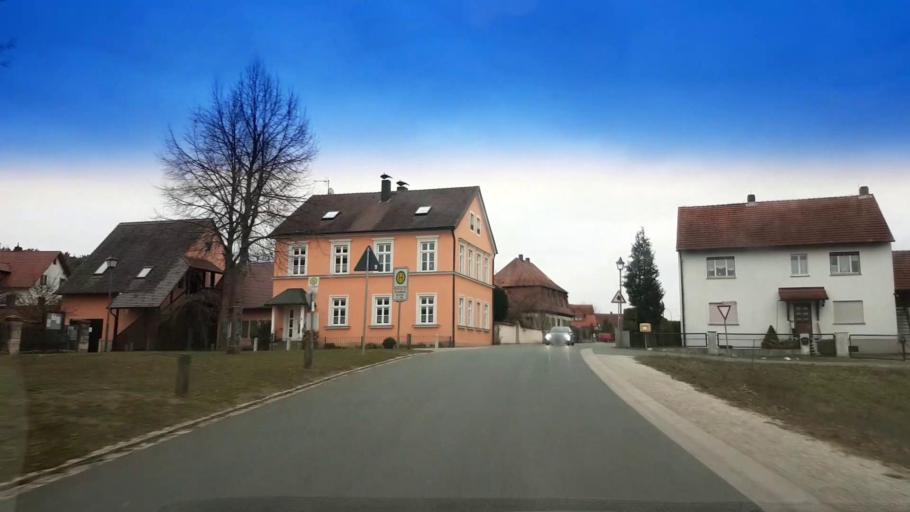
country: DE
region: Bavaria
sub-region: Upper Franconia
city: Pettstadt
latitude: 49.7909
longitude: 10.9090
